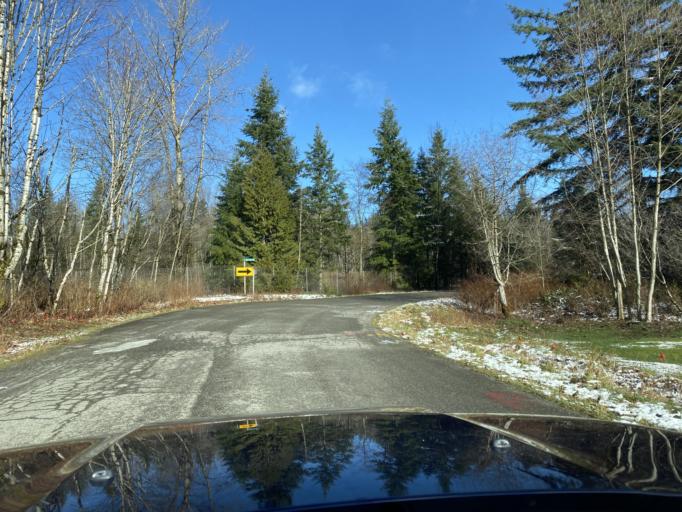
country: US
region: Washington
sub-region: King County
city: Snoqualmie
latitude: 47.5087
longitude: -121.8765
